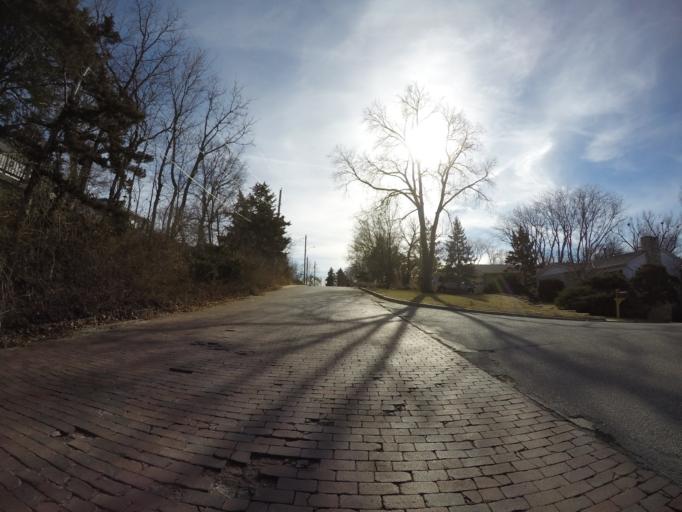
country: US
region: Kansas
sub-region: Riley County
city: Manhattan
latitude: 39.1775
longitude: -96.5866
